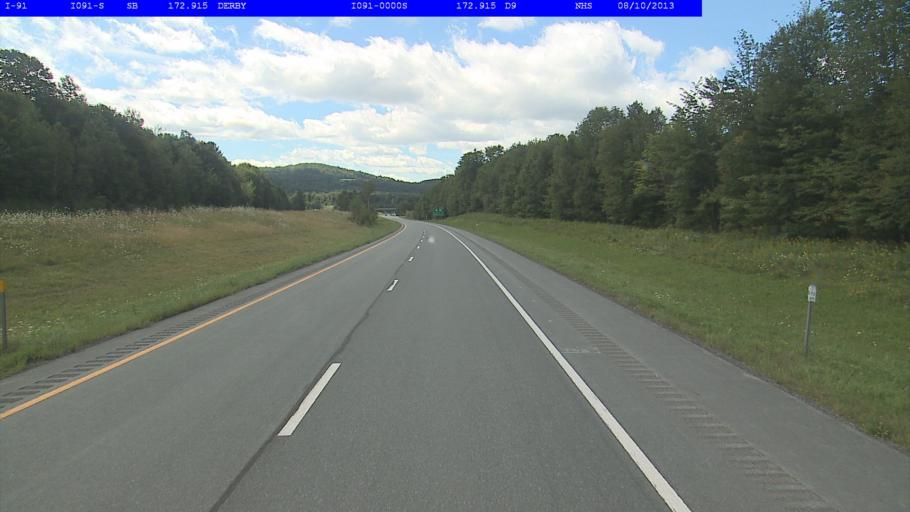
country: US
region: Vermont
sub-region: Orleans County
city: Newport
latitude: 44.9598
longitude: -72.1486
